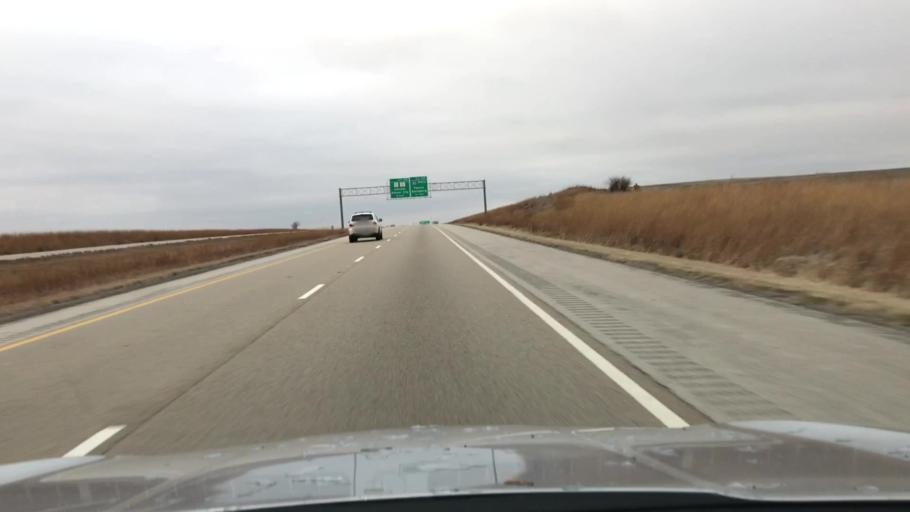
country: US
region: Illinois
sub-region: Logan County
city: Lincoln
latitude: 40.1817
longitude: -89.3924
